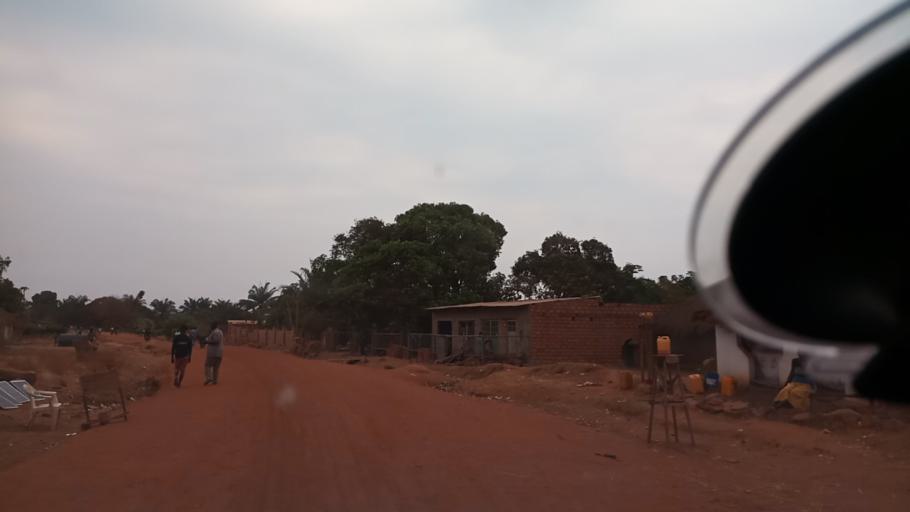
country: ZM
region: Luapula
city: Nchelenge
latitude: -9.2769
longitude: 28.3319
